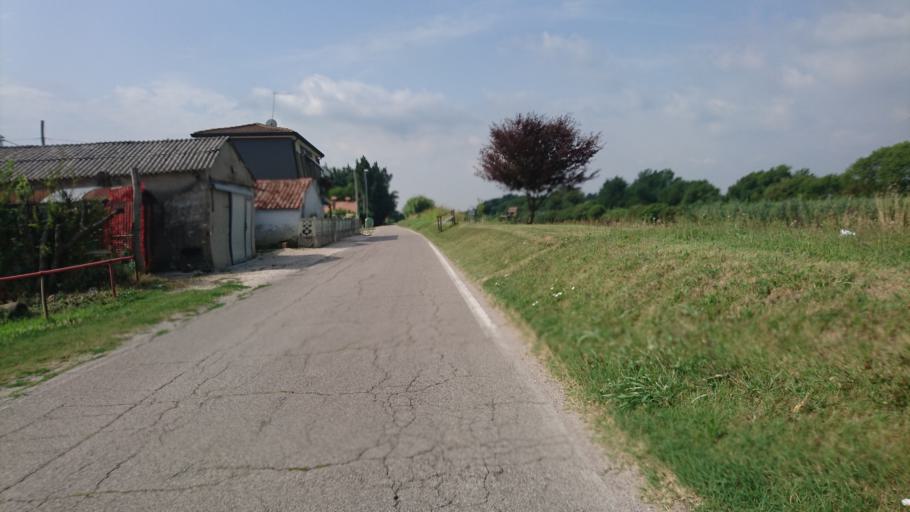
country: IT
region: Veneto
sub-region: Provincia di Venezia
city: Sant'Anna
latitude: 45.1677
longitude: 12.2718
